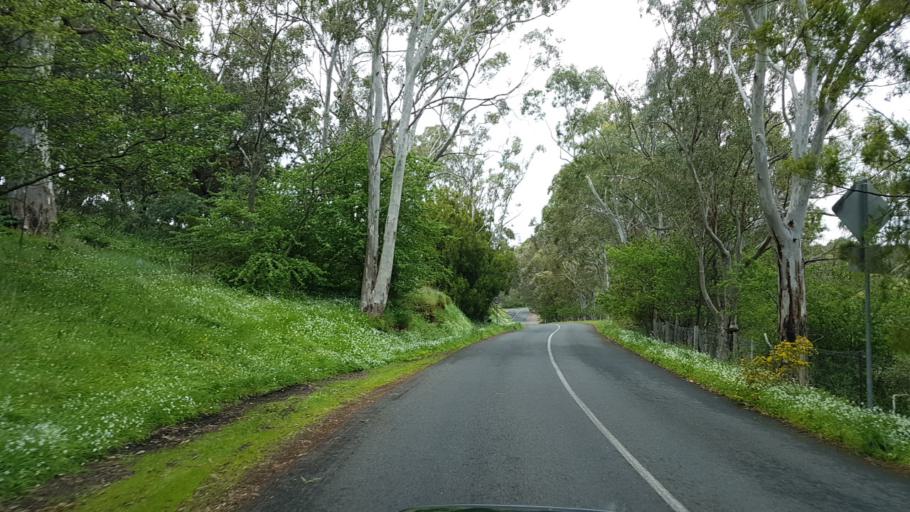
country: AU
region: South Australia
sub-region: Adelaide Hills
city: Adelaide Hills
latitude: -34.8897
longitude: 138.7493
